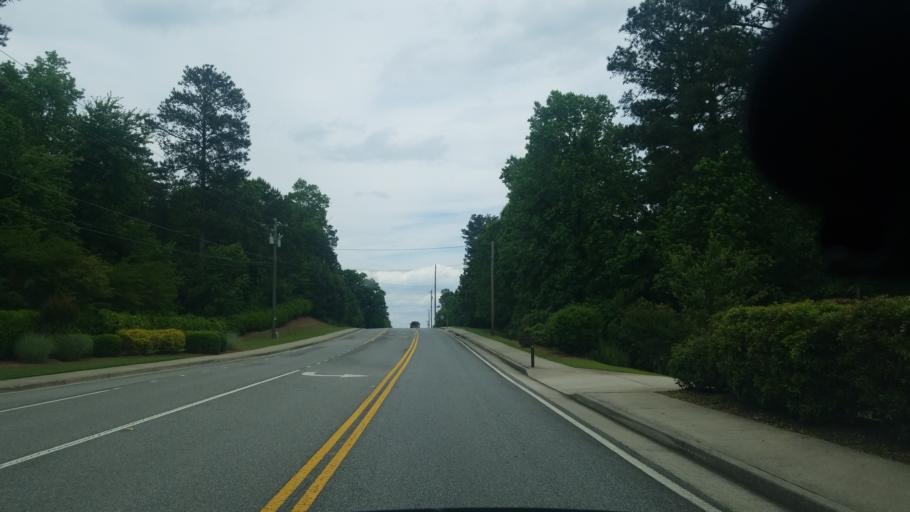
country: US
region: Georgia
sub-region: Forsyth County
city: Cumming
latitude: 34.1958
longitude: -84.1154
